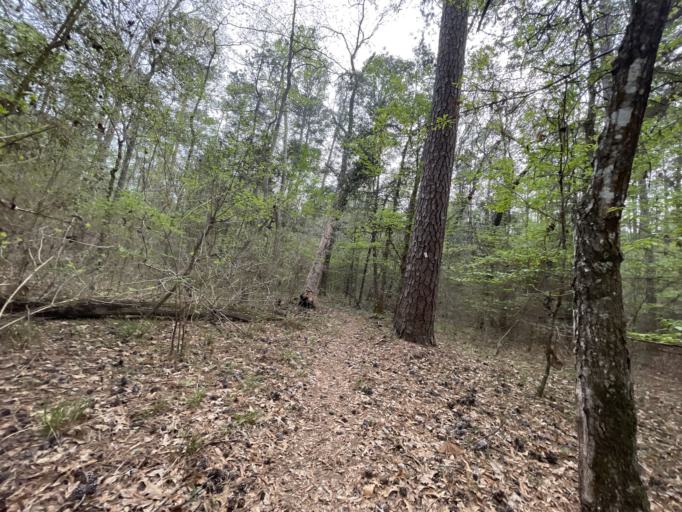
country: US
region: Texas
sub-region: Walker County
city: Huntsville
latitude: 30.6585
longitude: -95.4844
